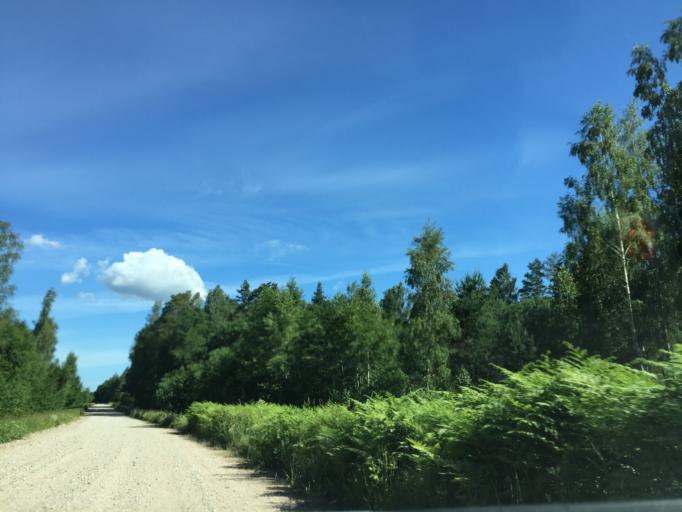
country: LV
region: Dundaga
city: Dundaga
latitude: 57.3381
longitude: 22.0303
